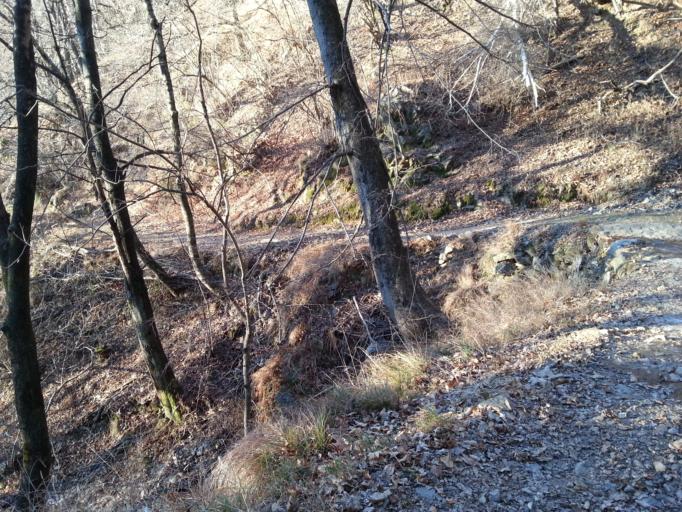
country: CH
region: Ticino
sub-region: Lugano District
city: Gravesano
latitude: 46.0462
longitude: 8.8769
